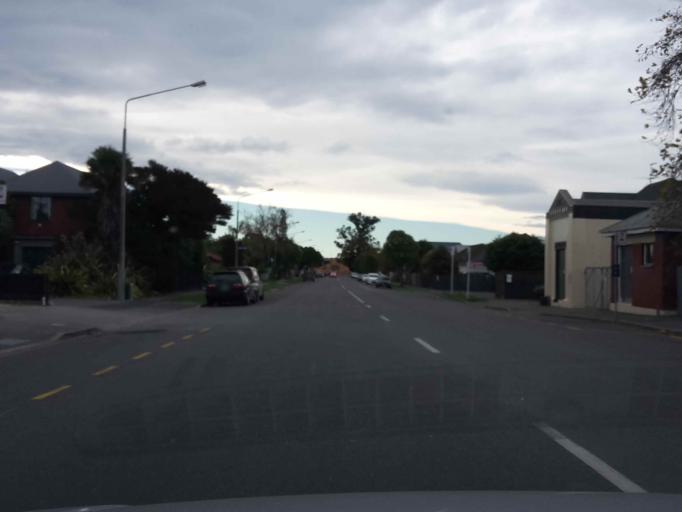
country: NZ
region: Canterbury
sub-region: Christchurch City
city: Christchurch
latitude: -43.5327
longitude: 172.6065
